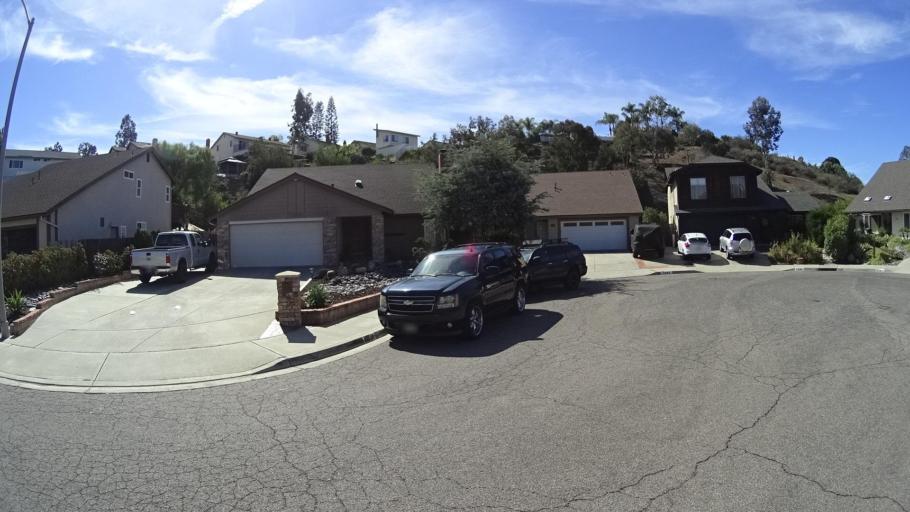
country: US
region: California
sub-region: San Diego County
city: Rancho San Diego
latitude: 32.7508
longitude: -116.9512
